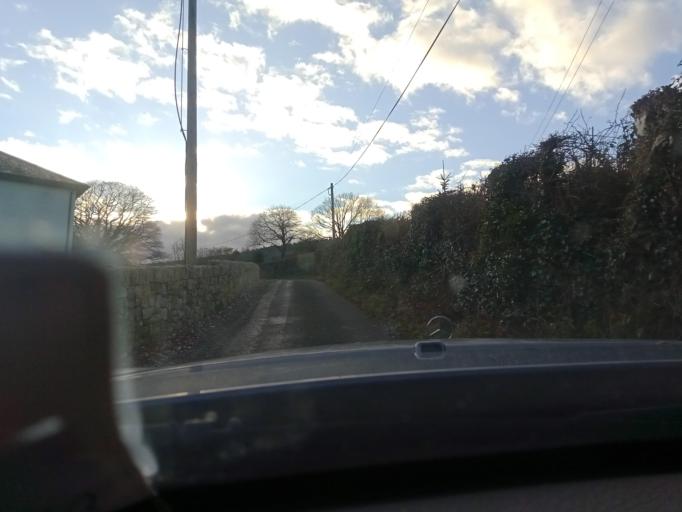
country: IE
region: Leinster
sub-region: Kilkenny
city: Graiguenamanagh
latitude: 52.5033
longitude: -6.9426
